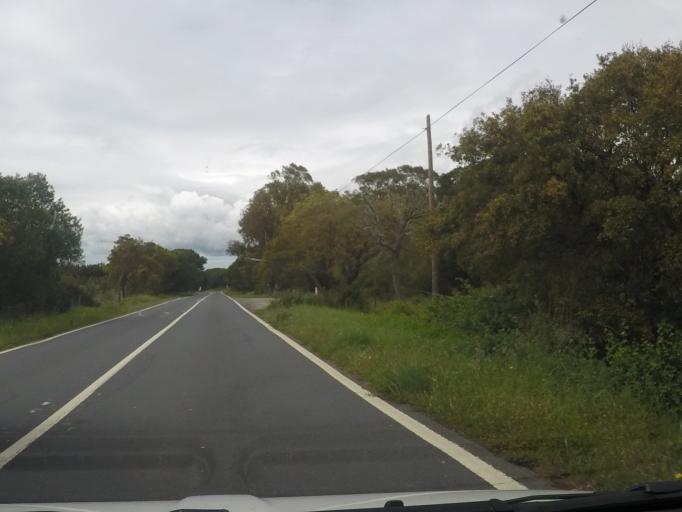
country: PT
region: Setubal
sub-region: Sines
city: Porto Covo
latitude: 37.8742
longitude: -8.7426
